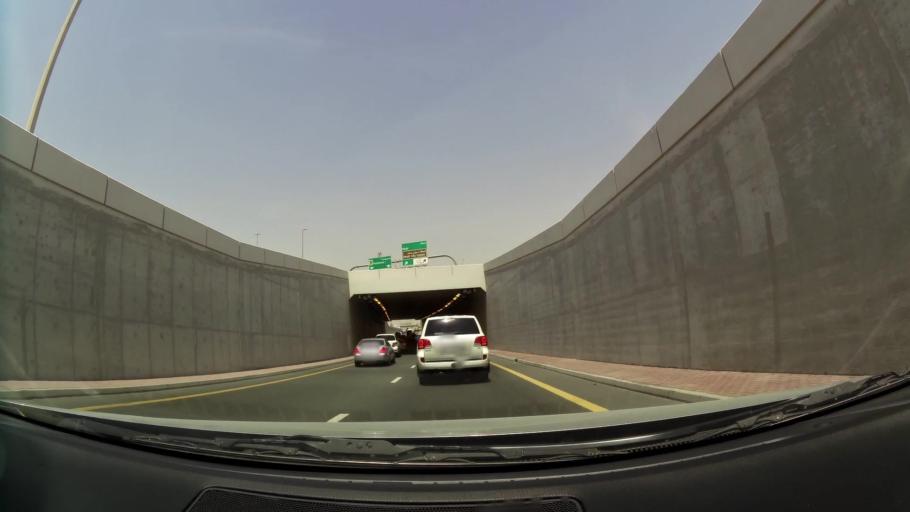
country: AE
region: Ash Shariqah
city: Sharjah
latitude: 25.2346
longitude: 55.4107
